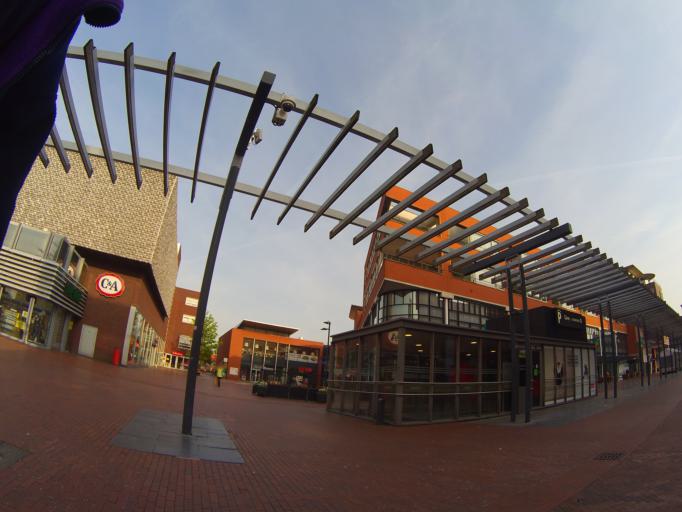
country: NL
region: North Holland
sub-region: Gemeente Amstelveen
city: Amstelveen
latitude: 52.3036
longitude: 4.8608
